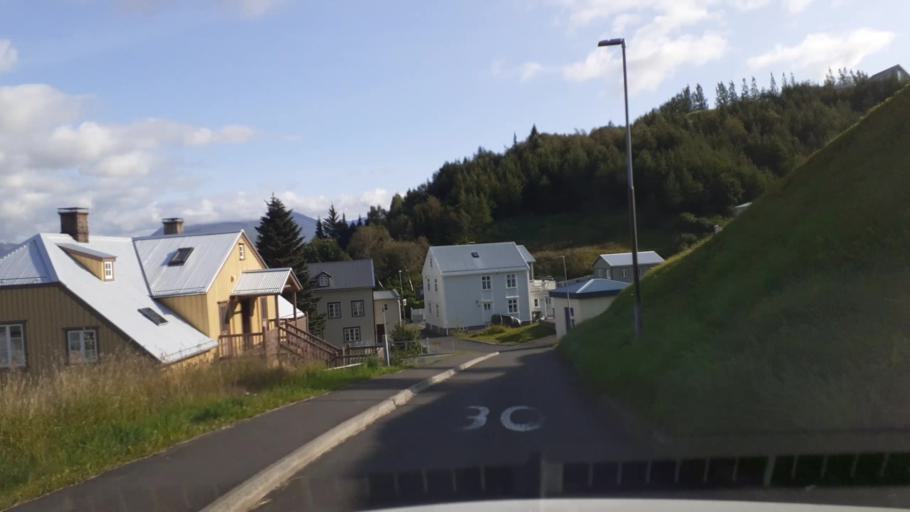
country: IS
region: Northeast
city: Akureyri
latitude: 65.6726
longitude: -18.0881
